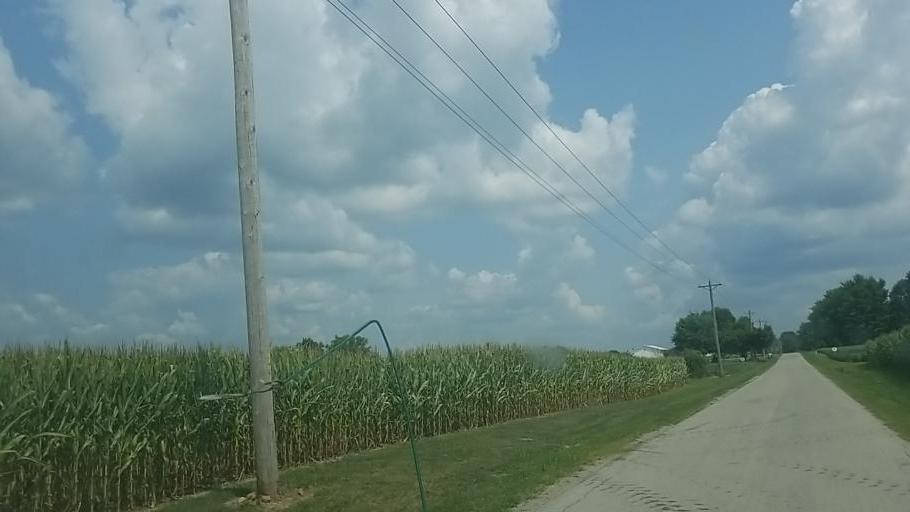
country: US
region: Ohio
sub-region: Wyandot County
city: Upper Sandusky
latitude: 40.9210
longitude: -83.1393
